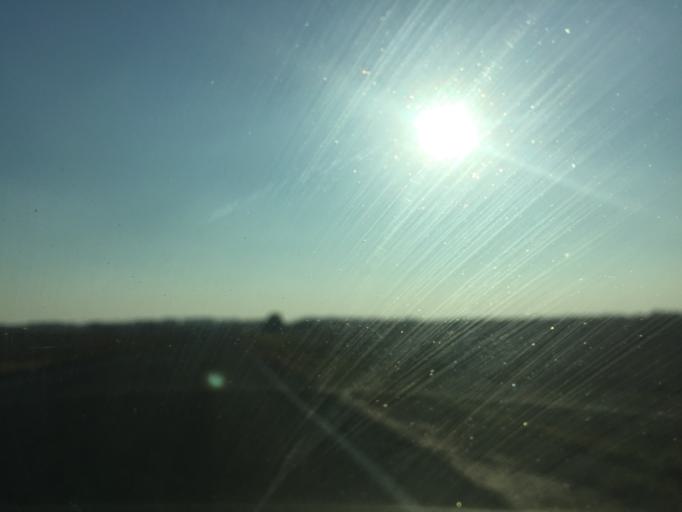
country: BY
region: Gomel
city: Dobrush
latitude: 52.3118
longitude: 31.2420
